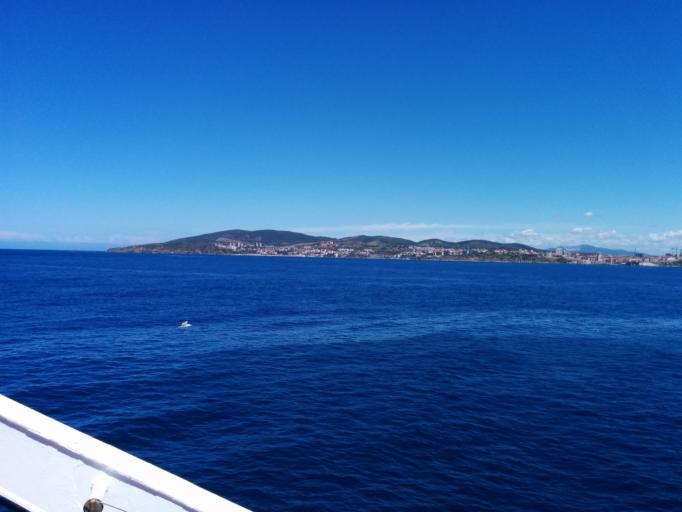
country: IT
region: Tuscany
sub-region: Provincia di Livorno
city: Piombino
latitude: 42.9005
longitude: 10.5115
